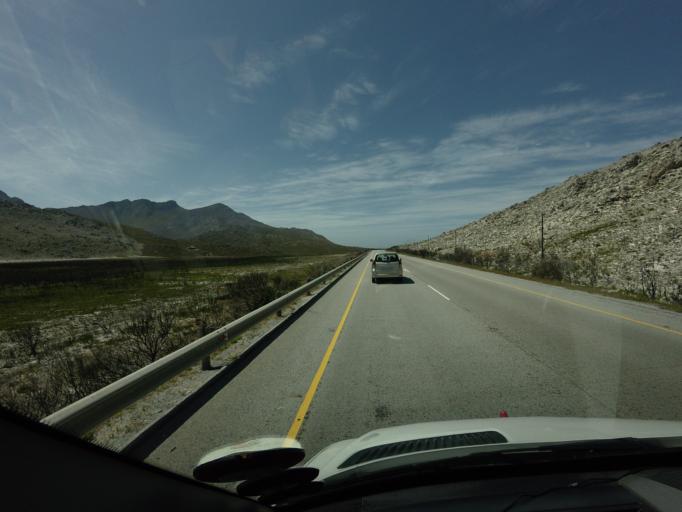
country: ZA
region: Western Cape
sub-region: Overberg District Municipality
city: Grabouw
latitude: -34.3189
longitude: 18.8318
